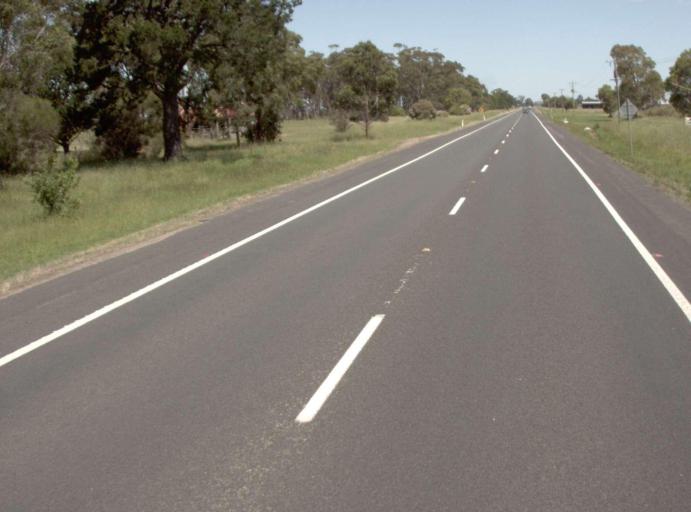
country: AU
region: Victoria
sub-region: Wellington
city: Sale
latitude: -38.0539
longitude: 147.0675
